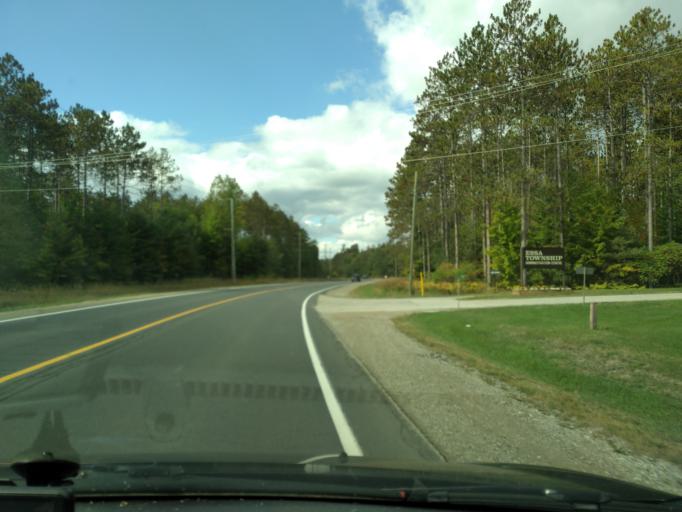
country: CA
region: Ontario
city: Angus
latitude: 44.2525
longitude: -79.8056
